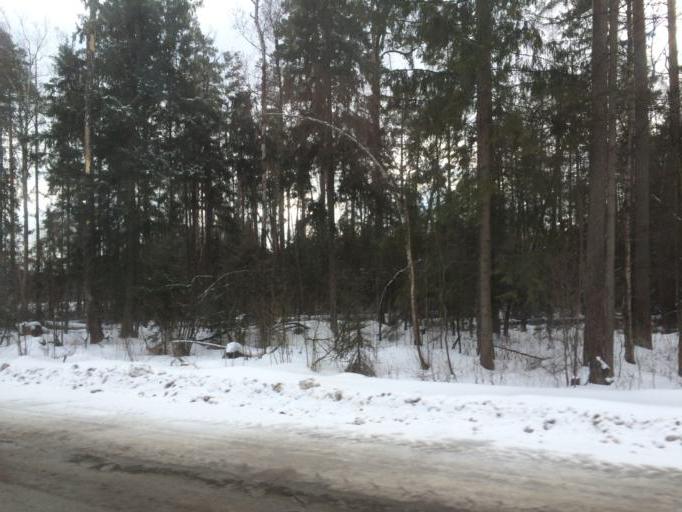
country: RU
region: Moskovskaya
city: Petrovo-Dal'neye
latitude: 55.7960
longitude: 37.1458
